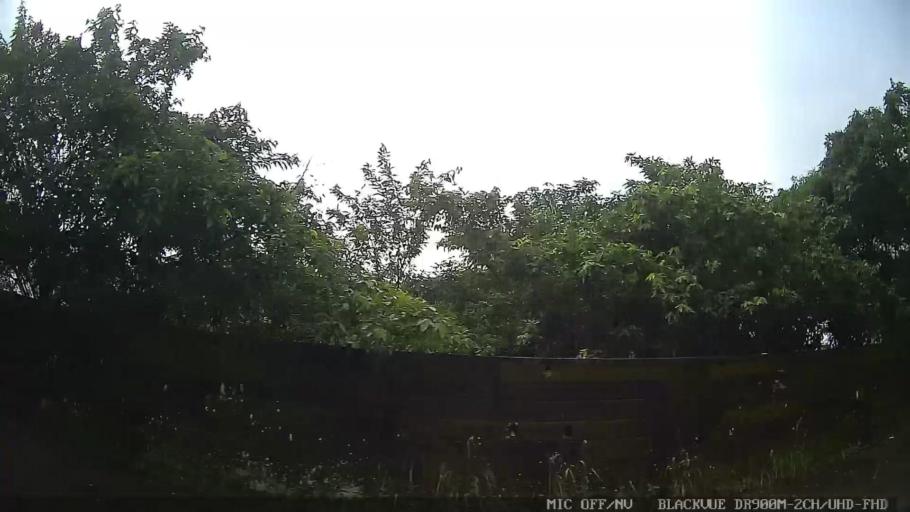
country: BR
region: Sao Paulo
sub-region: Itanhaem
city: Itanhaem
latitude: -24.1661
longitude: -46.7762
